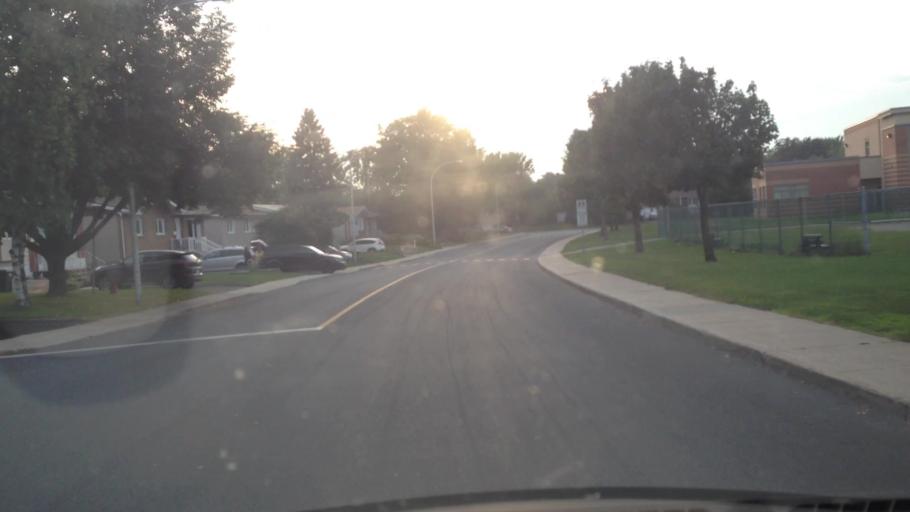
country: CA
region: Quebec
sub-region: Monteregie
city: Mercier
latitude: 45.3468
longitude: -73.7103
